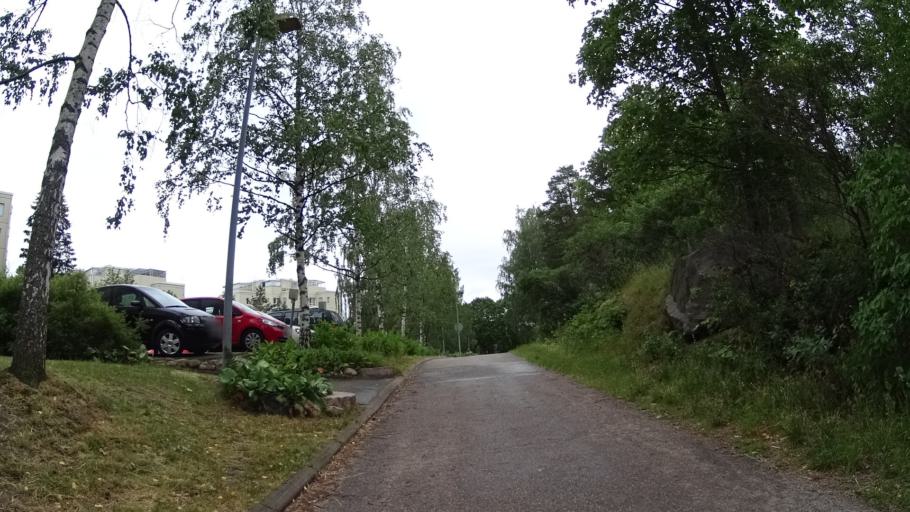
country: FI
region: Uusimaa
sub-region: Helsinki
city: Kilo
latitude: 60.2254
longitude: 24.8151
